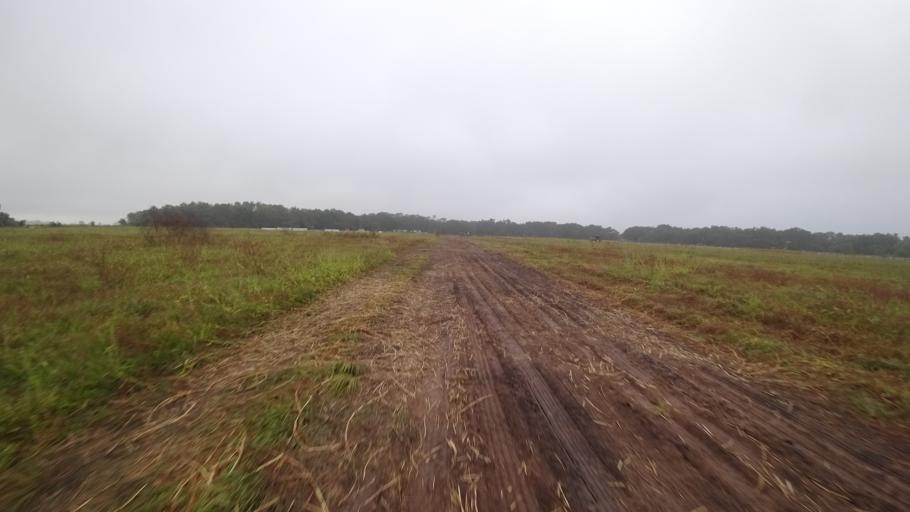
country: US
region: Florida
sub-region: Sarasota County
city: Lake Sarasota
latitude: 27.2922
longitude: -82.2160
